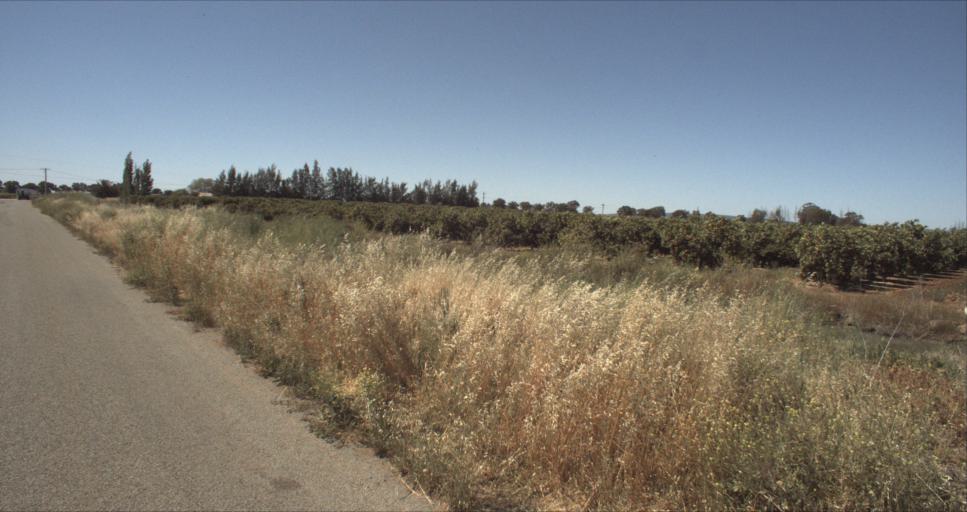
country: AU
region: New South Wales
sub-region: Leeton
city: Leeton
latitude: -34.5351
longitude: 146.3525
